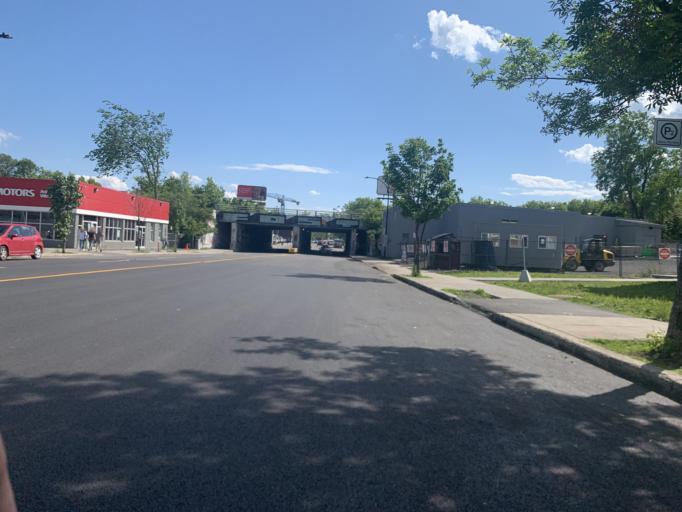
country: CA
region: Quebec
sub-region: Monteregie
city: Longueuil
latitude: 45.5405
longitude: -73.5554
